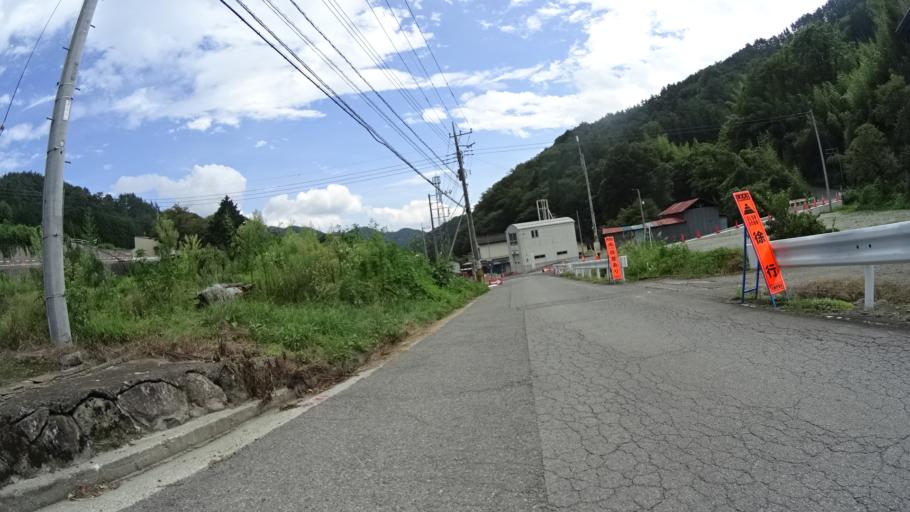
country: JP
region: Yamanashi
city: Kofu-shi
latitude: 35.7641
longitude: 138.5345
